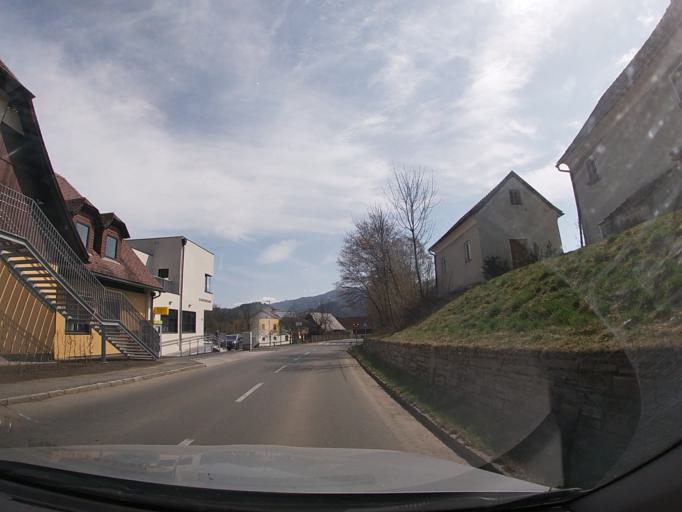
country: AT
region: Styria
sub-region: Politischer Bezirk Murtal
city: Feistritz bei Knittelfeld
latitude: 47.2683
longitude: 14.8907
